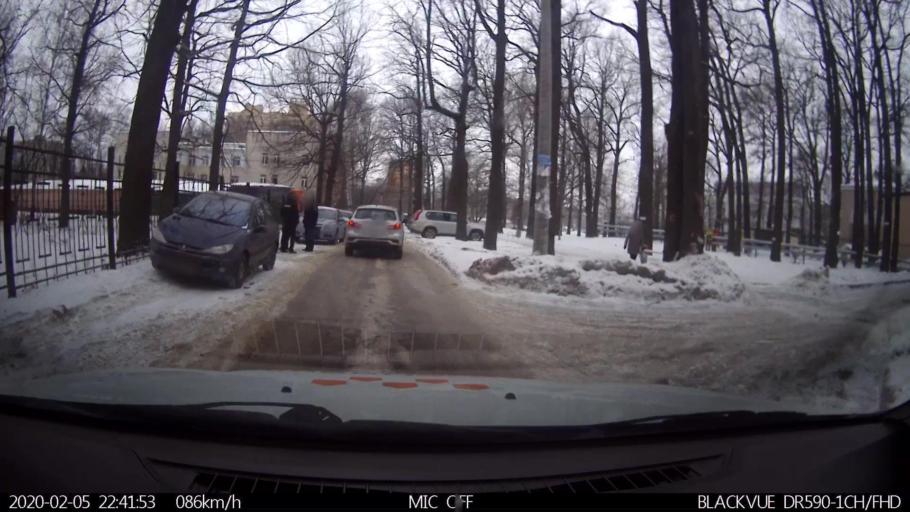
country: RU
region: Nizjnij Novgorod
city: Imeni Stepana Razina
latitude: 54.7196
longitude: 44.3466
